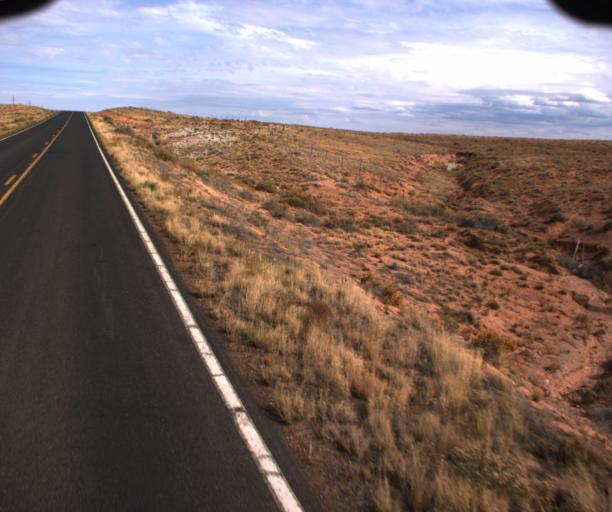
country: US
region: Arizona
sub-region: Apache County
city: Chinle
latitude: 35.9316
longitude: -109.6010
